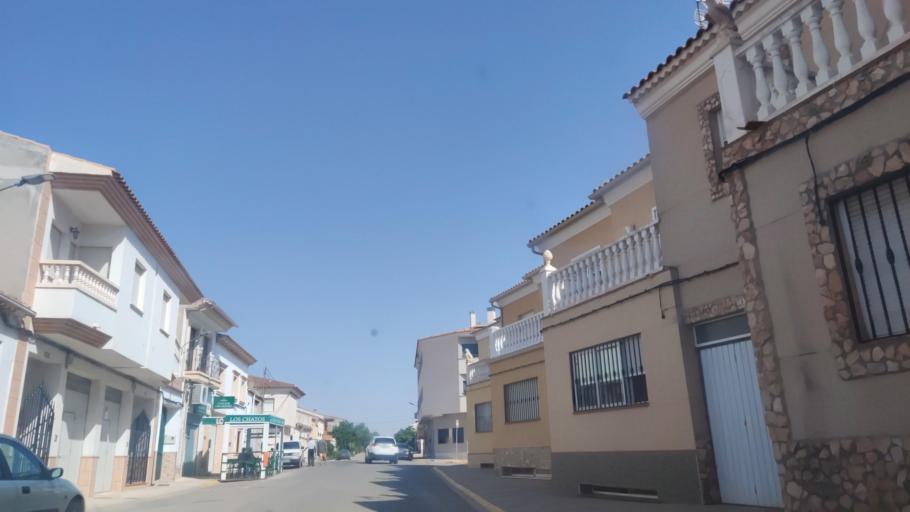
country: ES
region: Castille-La Mancha
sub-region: Provincia de Albacete
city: La Gineta
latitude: 39.1153
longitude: -1.9983
